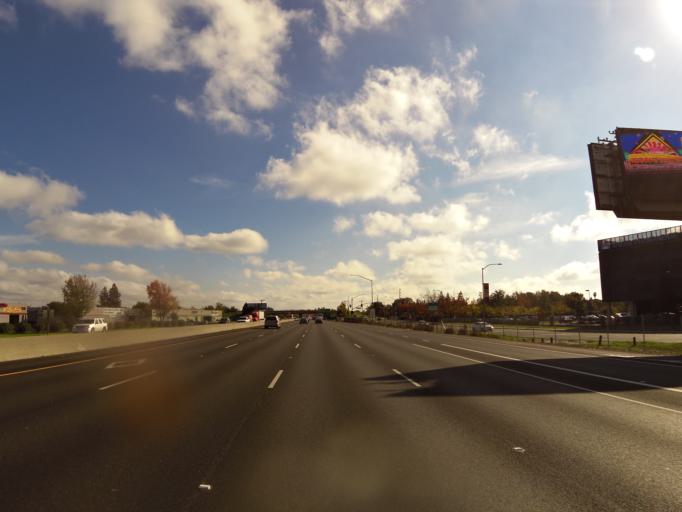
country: US
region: California
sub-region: Sacramento County
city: Florin
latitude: 38.4723
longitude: -121.4209
